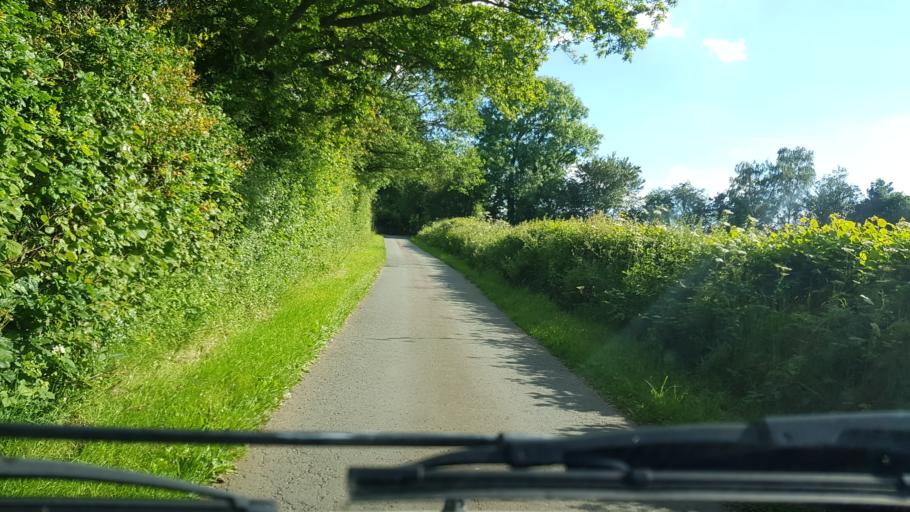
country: GB
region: England
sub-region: Worcestershire
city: Bewdley
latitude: 52.3444
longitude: -2.3296
